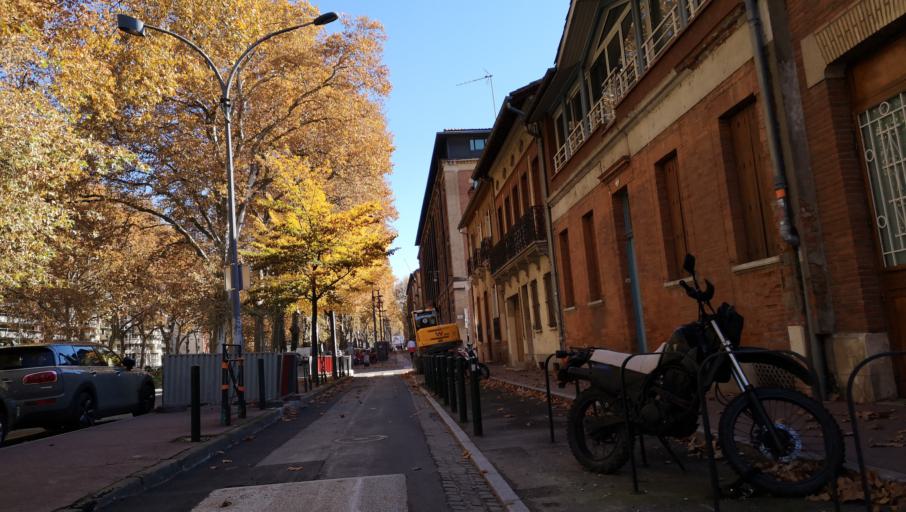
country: FR
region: Midi-Pyrenees
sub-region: Departement de la Haute-Garonne
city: Toulouse
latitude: 43.6064
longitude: 1.4301
